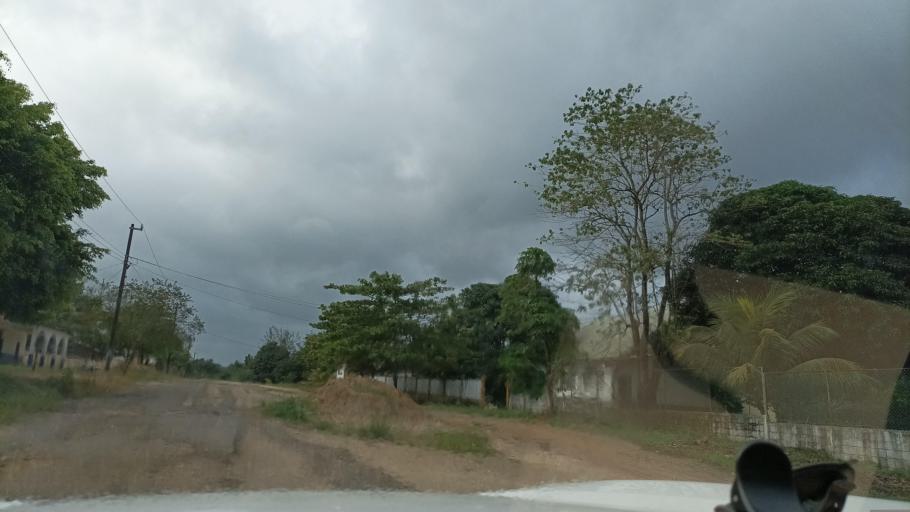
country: MX
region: Veracruz
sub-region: Moloacan
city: Cuichapa
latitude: 17.9233
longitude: -94.3683
